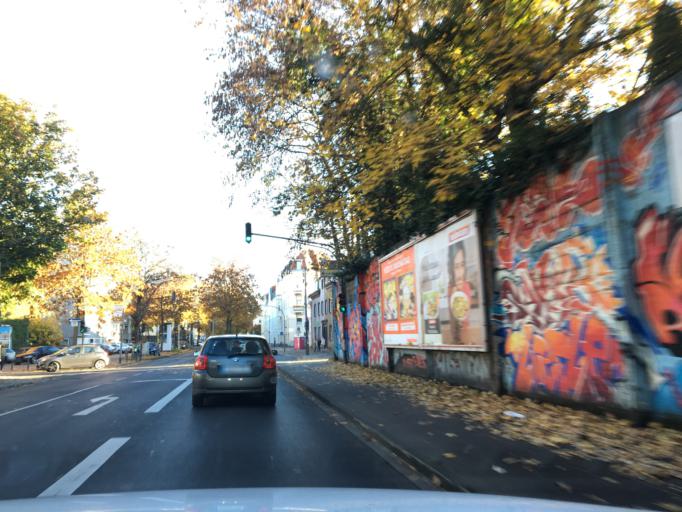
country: DE
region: North Rhine-Westphalia
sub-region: Regierungsbezirk Koln
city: Nippes
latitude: 50.9660
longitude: 6.9459
